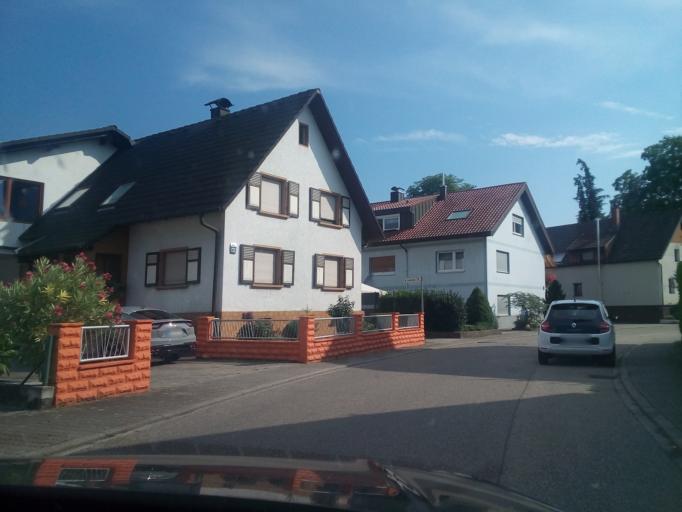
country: DE
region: Baden-Wuerttemberg
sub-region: Karlsruhe Region
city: Ottenhofen
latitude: 48.7593
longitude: 8.1407
